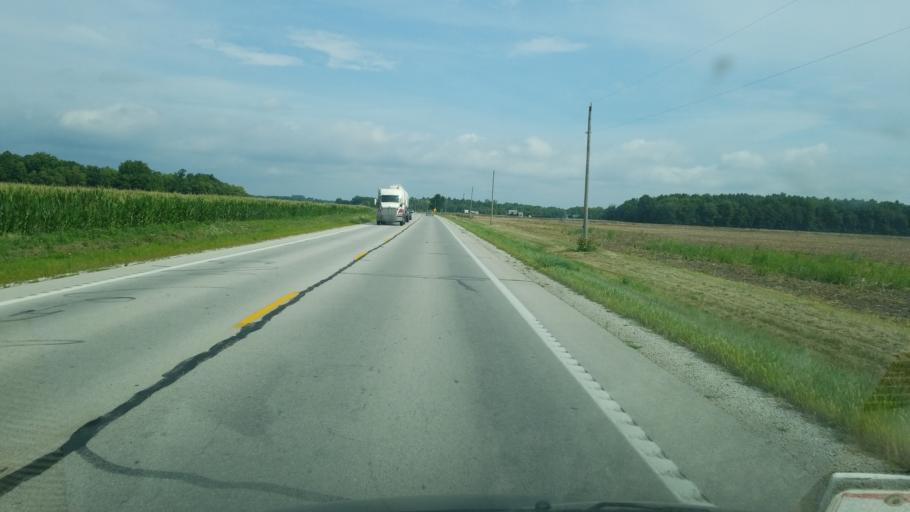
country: US
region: Ohio
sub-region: Sandusky County
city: Ballville
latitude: 41.2532
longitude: -83.1676
